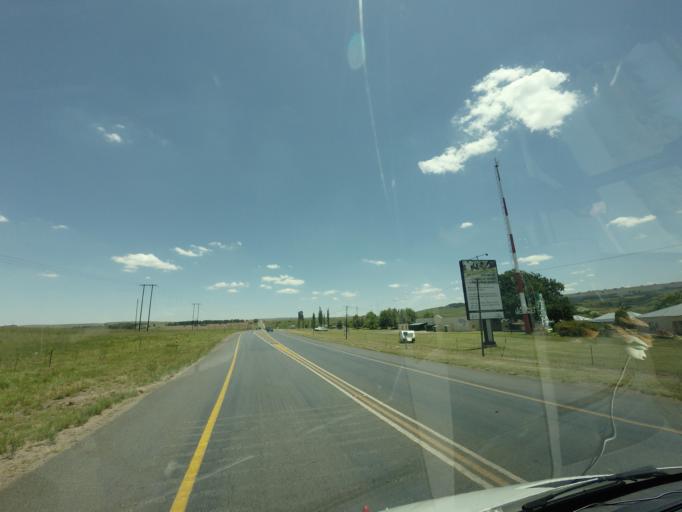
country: ZA
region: Mpumalanga
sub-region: Nkangala District Municipality
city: Belfast
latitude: -25.6878
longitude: 30.2154
